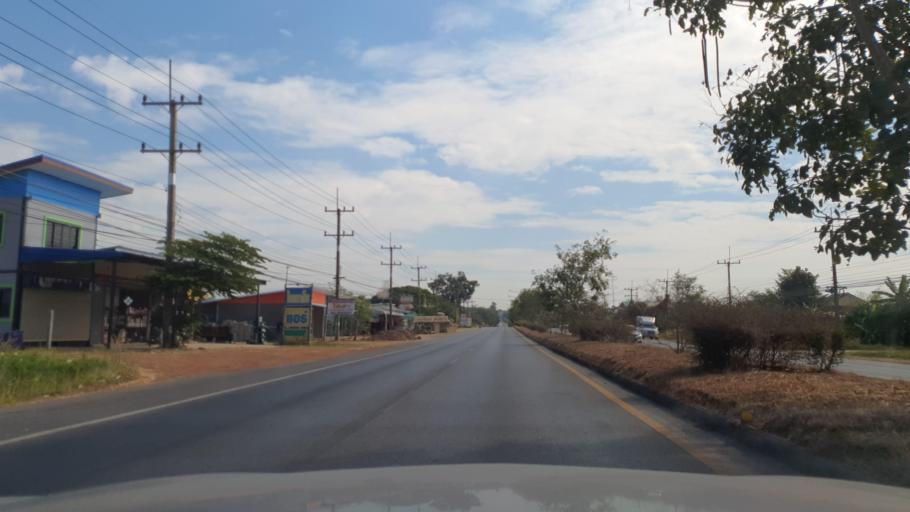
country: TH
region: Kalasin
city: Yang Talat
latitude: 16.4074
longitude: 103.4039
